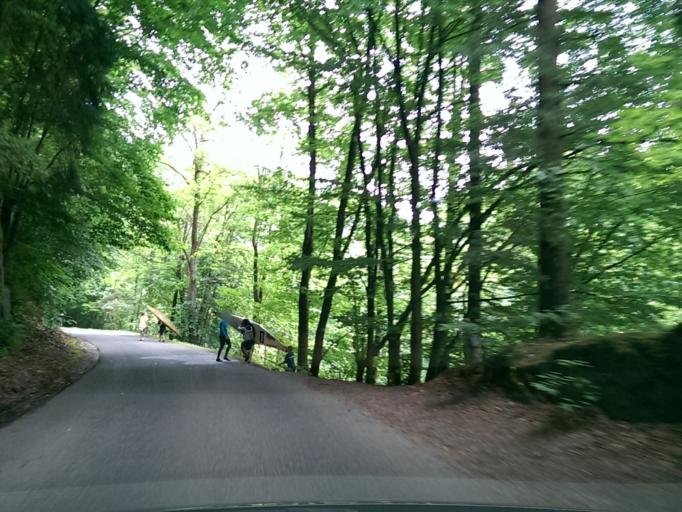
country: CZ
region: Liberecky
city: Zelezny Brod
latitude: 50.6357
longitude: 15.2883
